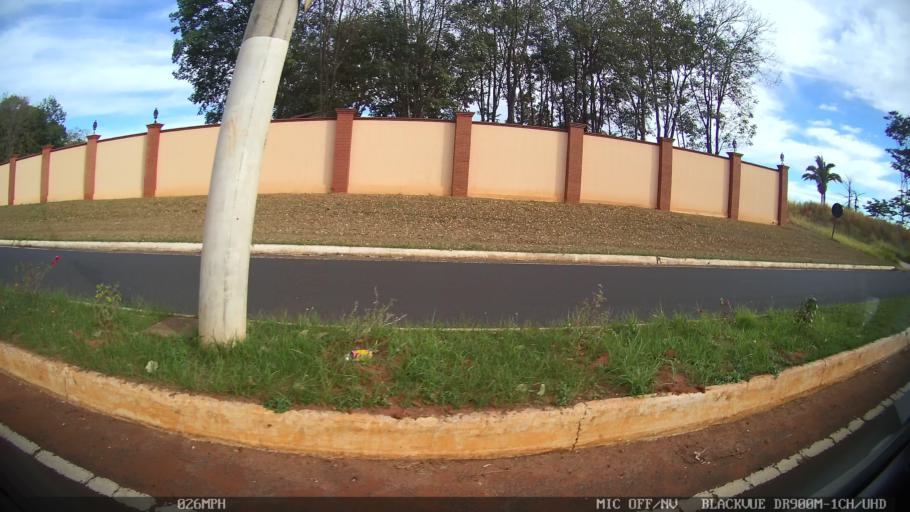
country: BR
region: Sao Paulo
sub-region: Catanduva
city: Catanduva
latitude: -21.1101
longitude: -48.9615
